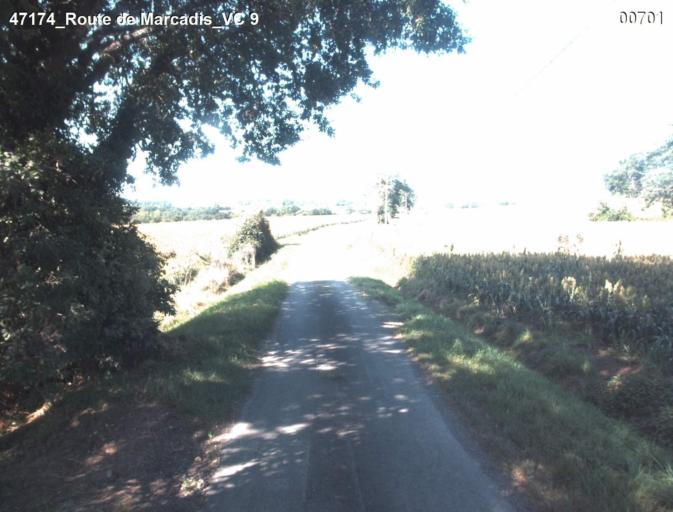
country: FR
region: Midi-Pyrenees
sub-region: Departement du Gers
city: Condom
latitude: 44.0205
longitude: 0.3427
